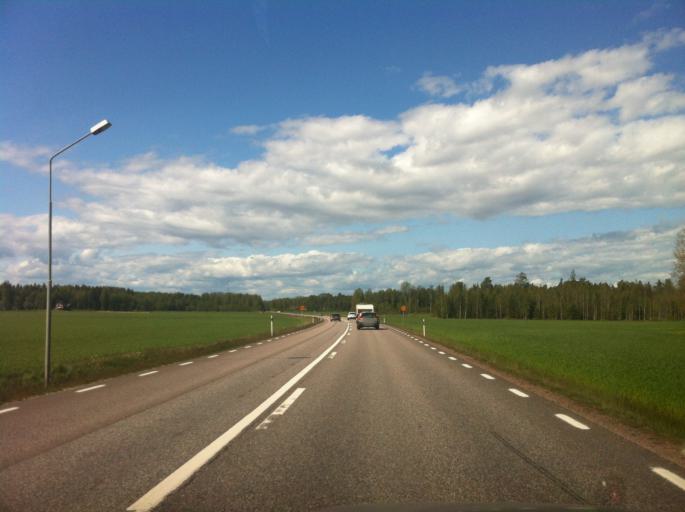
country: SE
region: Vaermland
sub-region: Kristinehamns Kommun
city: Bjorneborg
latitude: 59.1322
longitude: 14.1779
